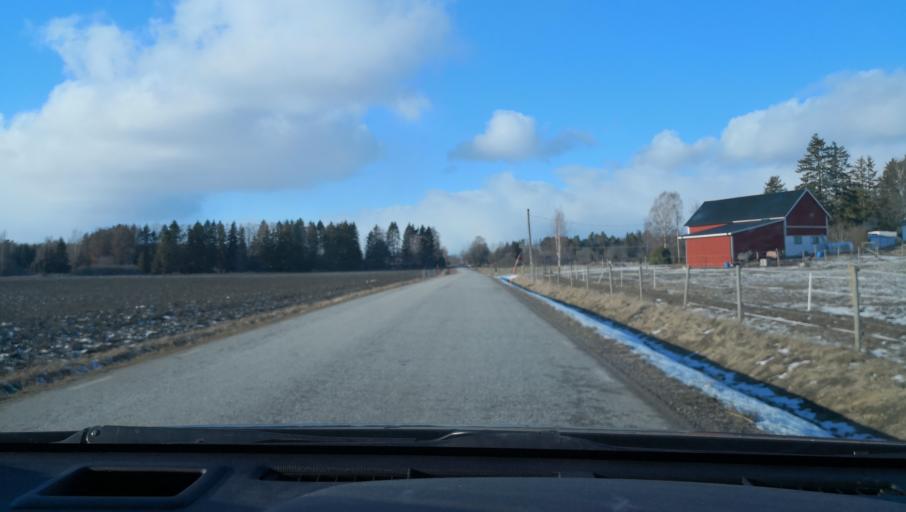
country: SE
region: Uppsala
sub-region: Enkopings Kommun
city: Hummelsta
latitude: 59.6327
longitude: 16.9752
